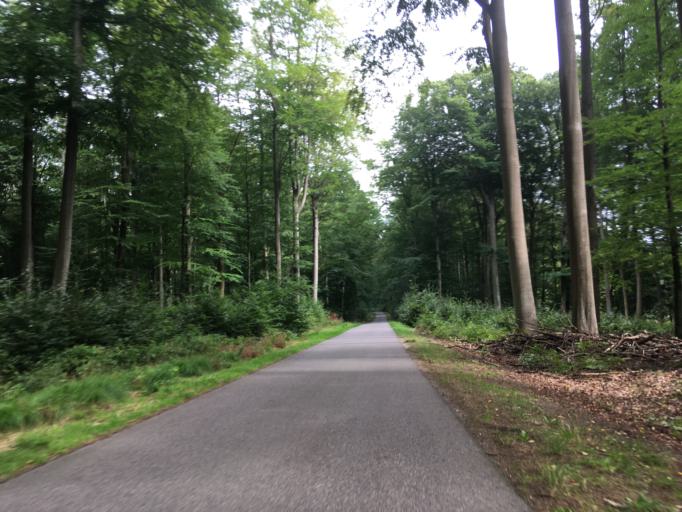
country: DE
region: Brandenburg
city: Althuttendorf
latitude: 53.0192
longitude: 13.8012
